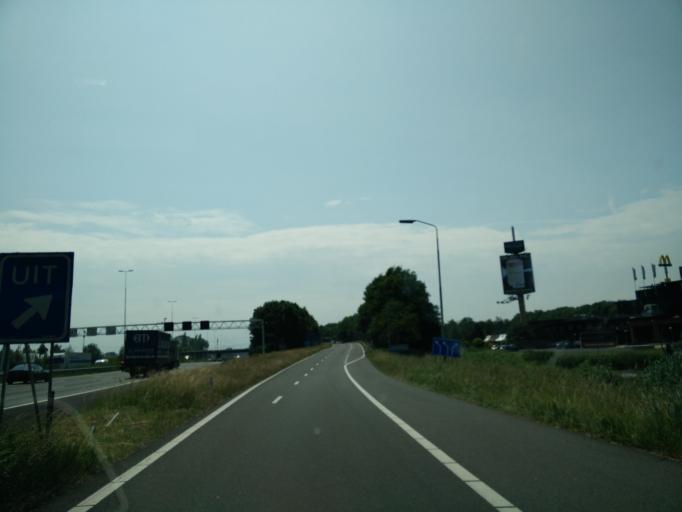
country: NL
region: South Holland
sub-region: Gemeente Dordrecht
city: Dordrecht
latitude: 51.7760
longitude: 4.6495
